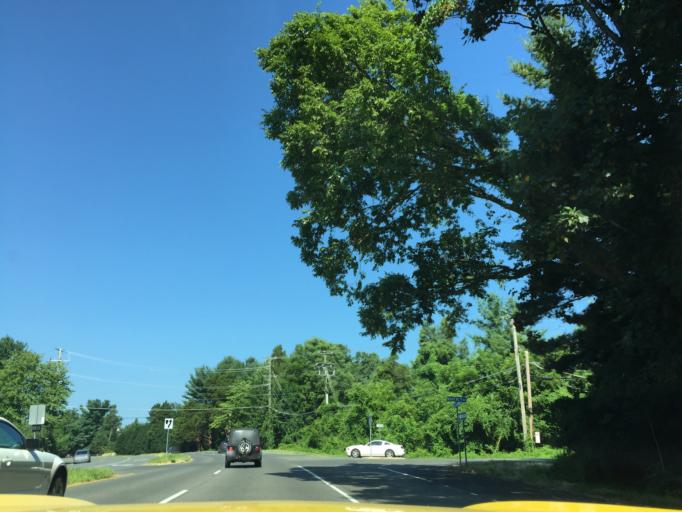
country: US
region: Virginia
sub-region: Fairfax County
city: McLean
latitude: 38.9427
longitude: -77.1655
